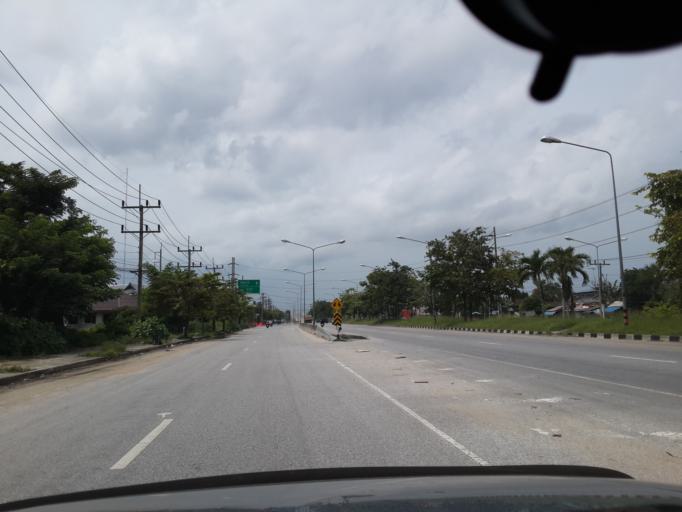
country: TH
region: Pattani
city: Pattani
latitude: 6.8514
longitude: 101.2562
